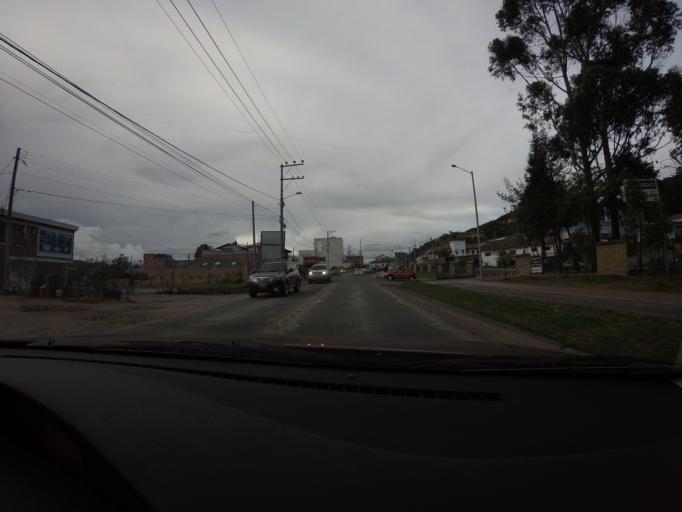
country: CO
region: Cundinamarca
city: Sopo
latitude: 4.9129
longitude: -73.9427
